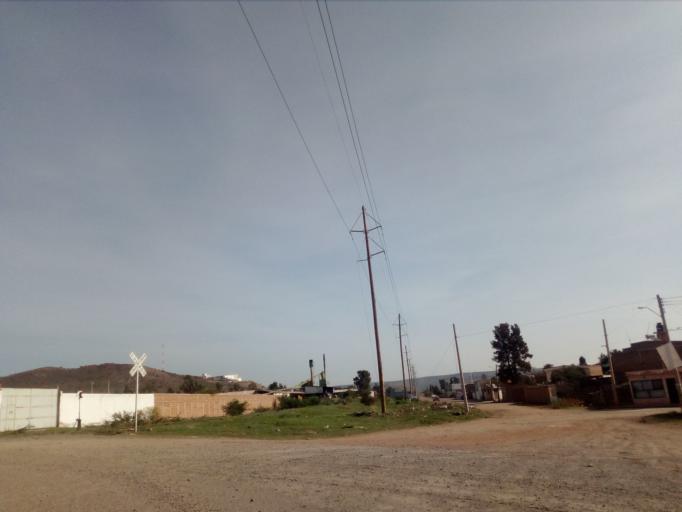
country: MX
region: Durango
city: Victoria de Durango
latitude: 24.0543
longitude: -104.6549
